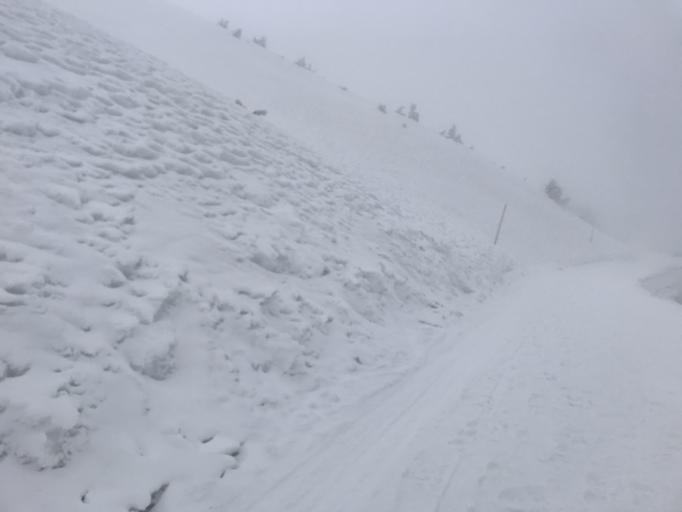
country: IT
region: Trentino-Alto Adige
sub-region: Bolzano
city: San Pietro
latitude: 46.6872
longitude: 11.7276
